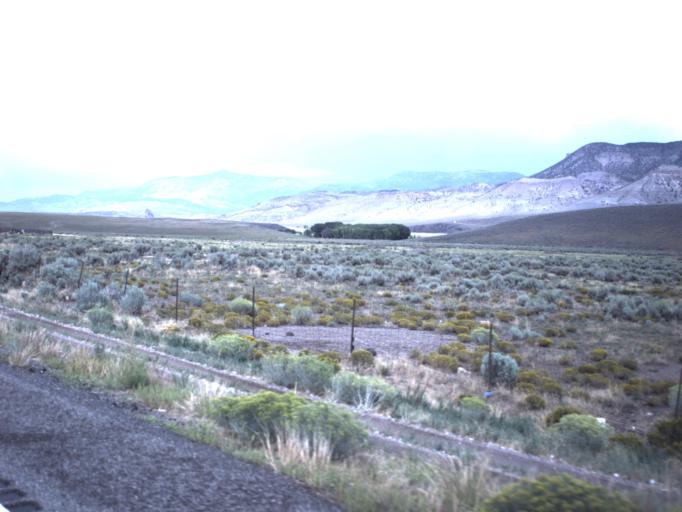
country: US
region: Utah
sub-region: Piute County
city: Junction
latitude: 38.2601
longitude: -112.2208
